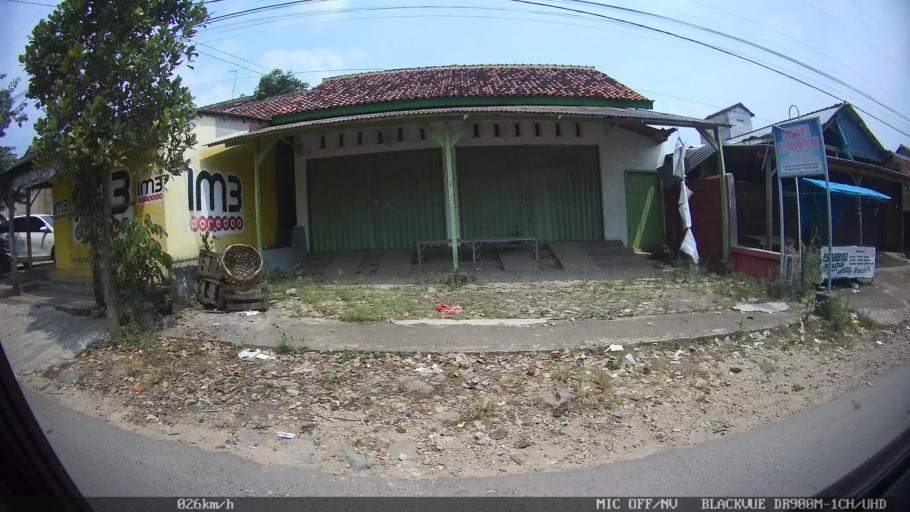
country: ID
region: Lampung
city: Gadingrejo
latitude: -5.3758
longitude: 105.0557
